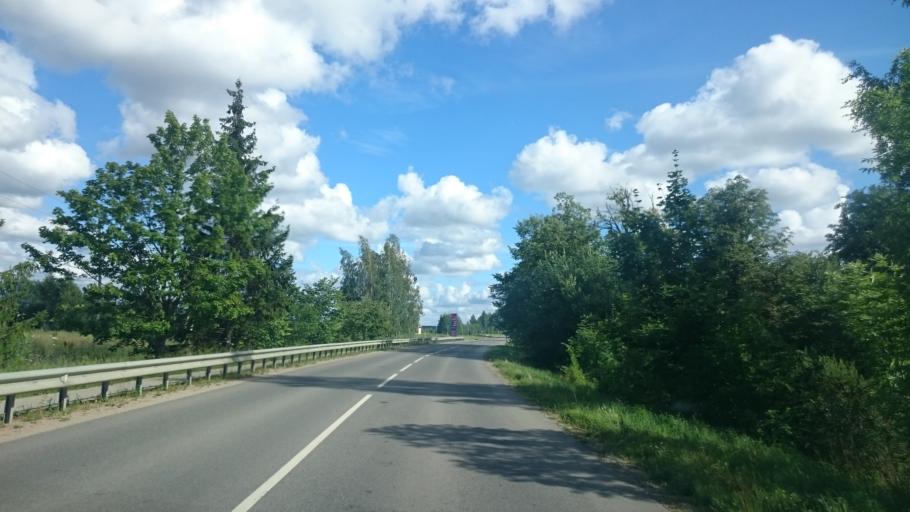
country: LV
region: Aizpute
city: Aizpute
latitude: 56.7060
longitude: 21.6239
